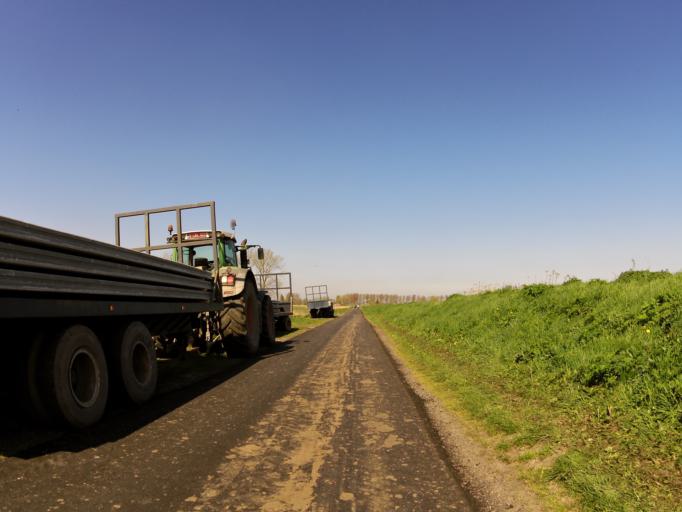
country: BE
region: Flanders
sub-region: Provincie West-Vlaanderen
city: Gistel
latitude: 51.1438
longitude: 2.9993
